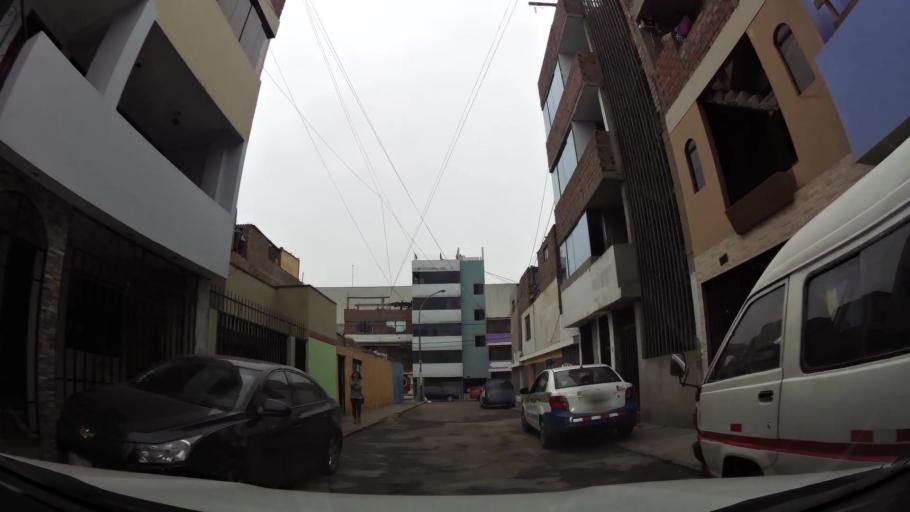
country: PE
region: Lima
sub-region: Lima
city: Surco
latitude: -12.1100
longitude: -77.0121
